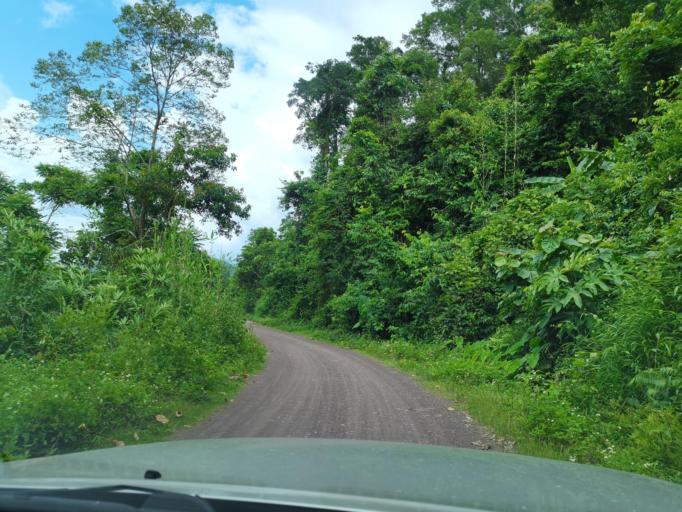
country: LA
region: Loungnamtha
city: Muang Long
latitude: 20.7033
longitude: 101.0126
